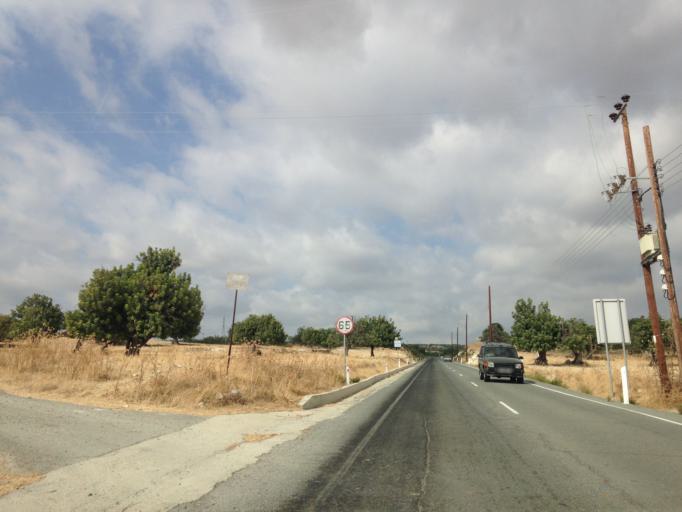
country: CY
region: Limassol
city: Pissouri
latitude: 34.7018
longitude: 32.7637
